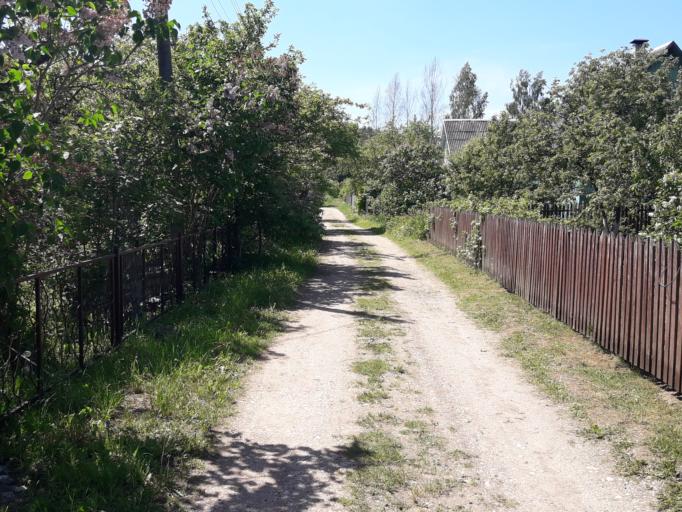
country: BY
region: Minsk
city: Pyatryshki
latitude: 54.1297
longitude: 27.1342
